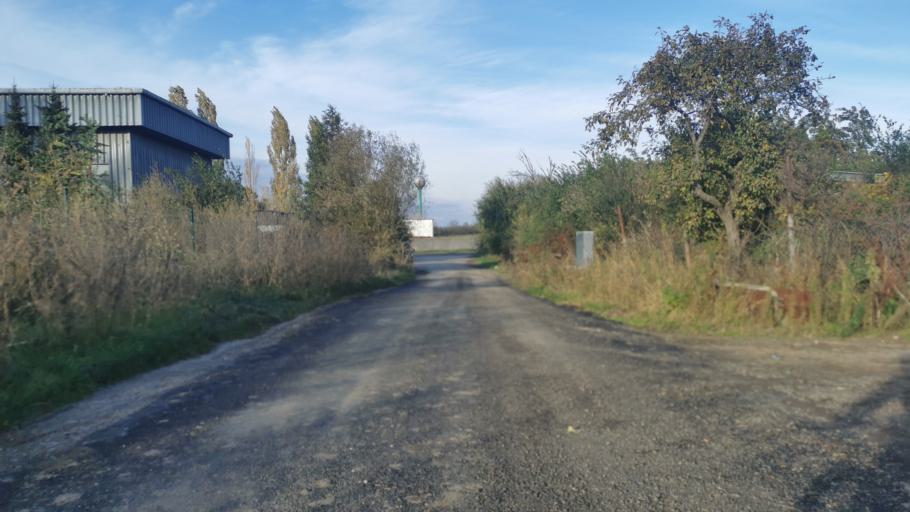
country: CZ
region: South Moravian
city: Sudomerice
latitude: 48.8460
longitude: 17.2551
